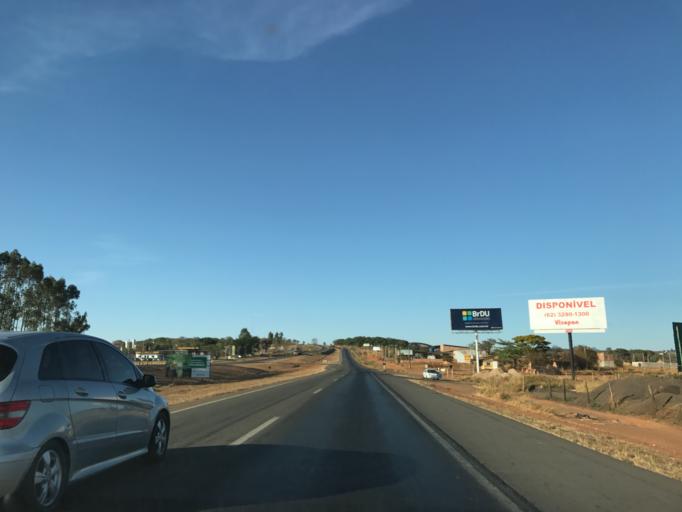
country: BR
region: Goias
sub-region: Aparecida De Goiania
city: Aparecida de Goiania
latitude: -16.8862
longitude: -49.2543
